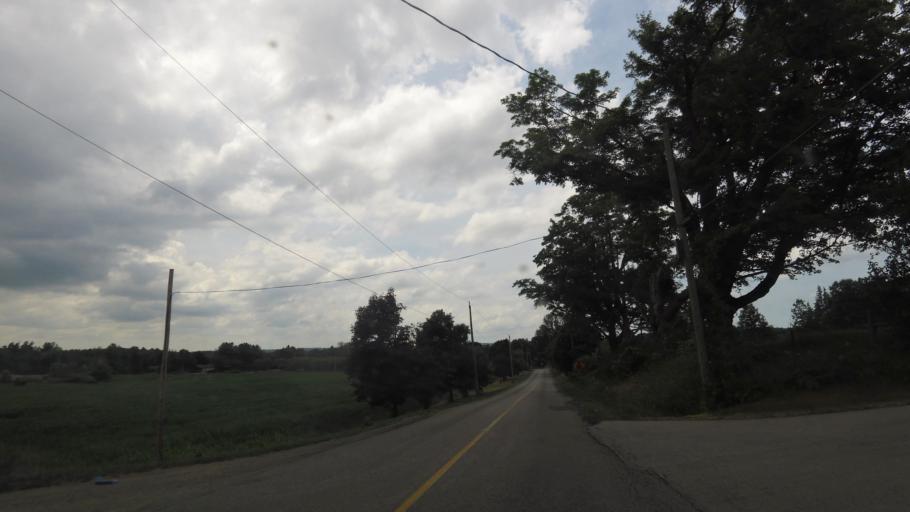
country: CA
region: Ontario
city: Brampton
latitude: 43.8374
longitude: -79.8702
